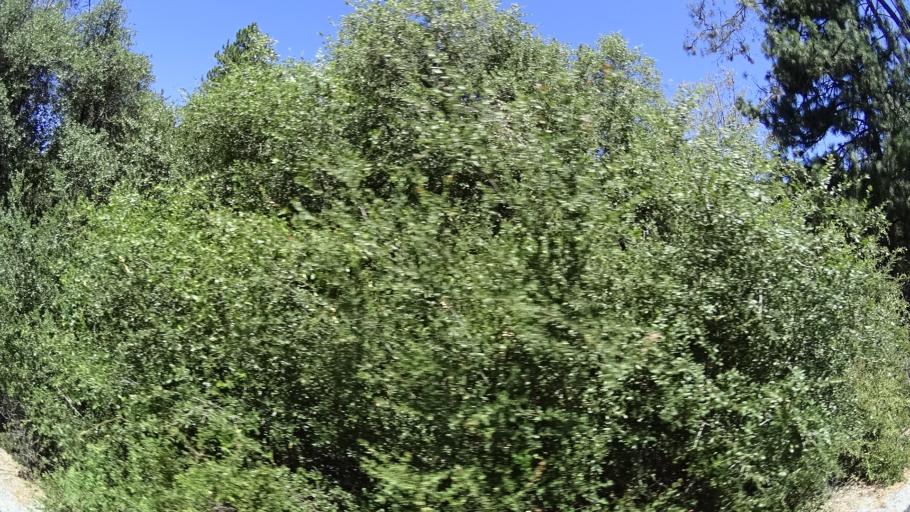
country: US
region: California
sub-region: Amador County
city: Pine Grove
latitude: 38.3399
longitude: -120.6095
